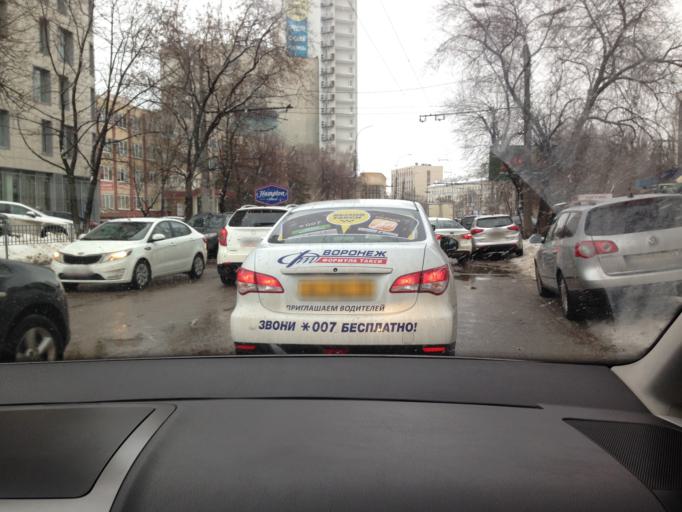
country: RU
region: Voronezj
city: Voronezh
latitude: 51.6735
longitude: 39.1824
